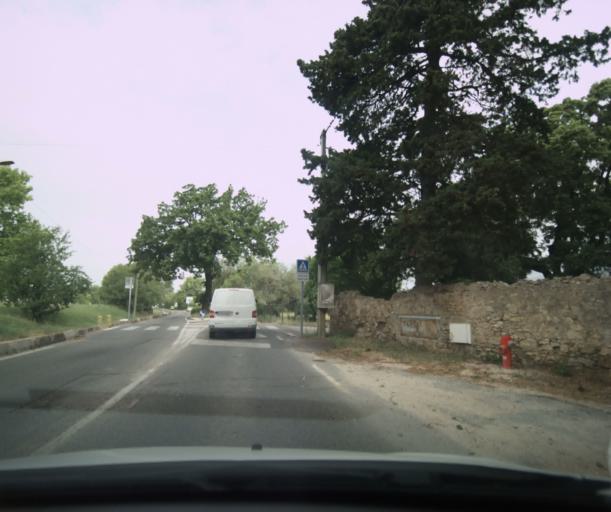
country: FR
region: Provence-Alpes-Cote d'Azur
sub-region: Departement du Var
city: Le Pradet
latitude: 43.1100
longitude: 6.0227
